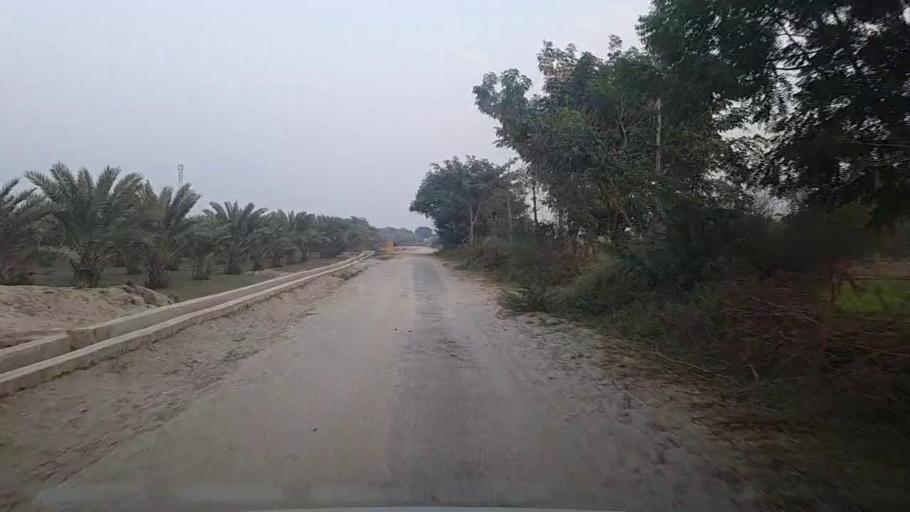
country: PK
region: Sindh
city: Kot Diji
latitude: 27.3458
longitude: 68.6365
